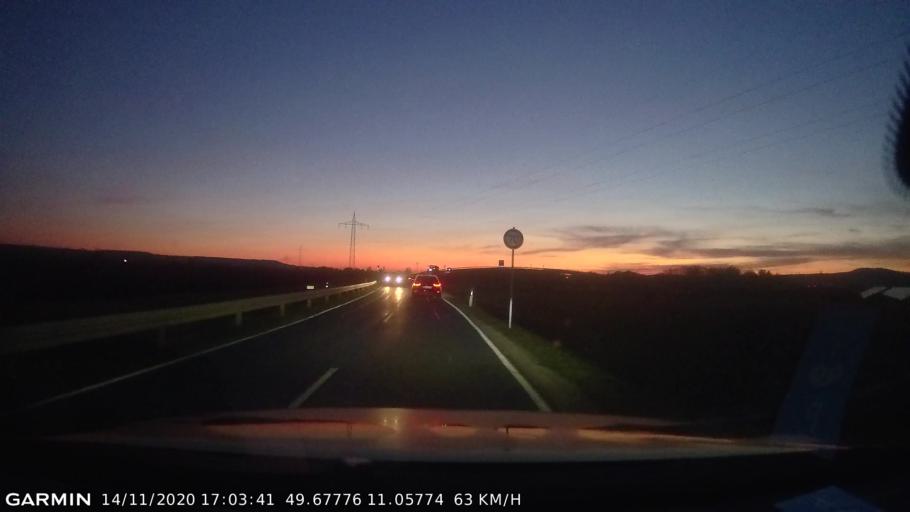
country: DE
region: Bavaria
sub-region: Upper Franconia
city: Poxdorf
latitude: 49.6778
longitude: 11.0578
